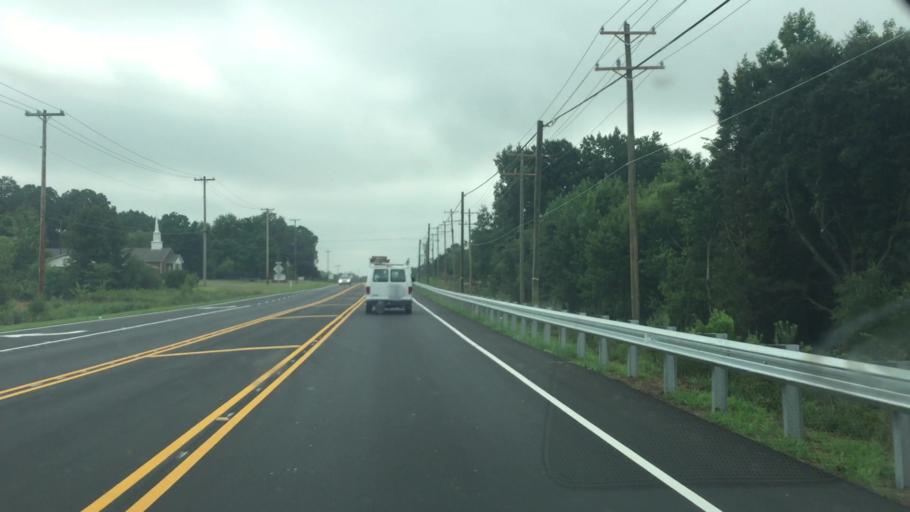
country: US
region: North Carolina
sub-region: Cabarrus County
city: Kannapolis
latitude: 35.4369
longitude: -80.6858
